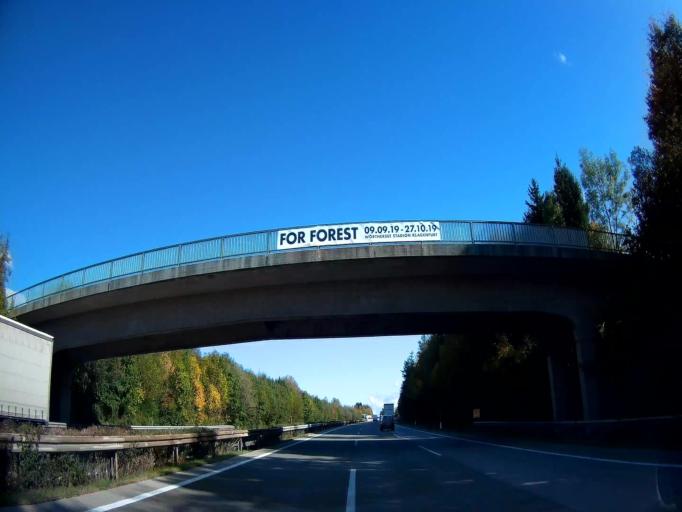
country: AT
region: Carinthia
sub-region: Politischer Bezirk Villach Land
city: Wernberg
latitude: 46.6236
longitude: 13.9289
